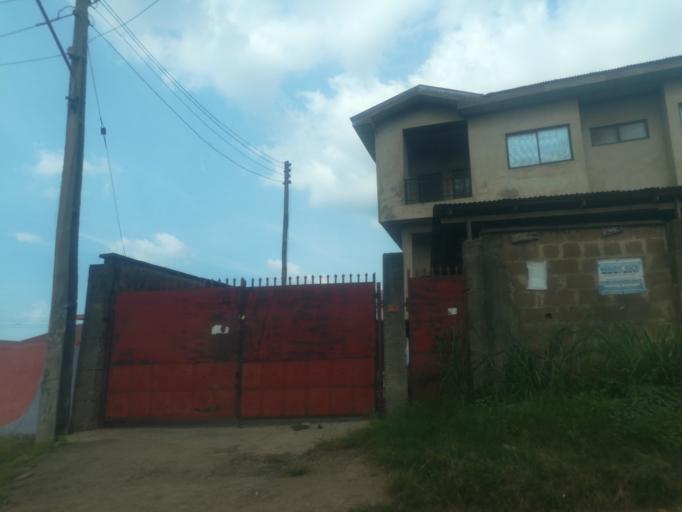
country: NG
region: Ogun
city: Abeokuta
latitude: 7.1246
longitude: 3.3225
